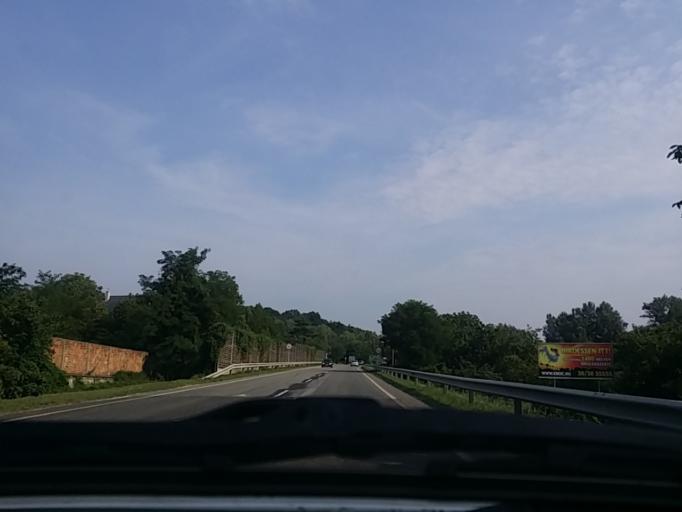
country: HU
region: Fejer
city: Szarliget
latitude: 47.5373
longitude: 18.4551
